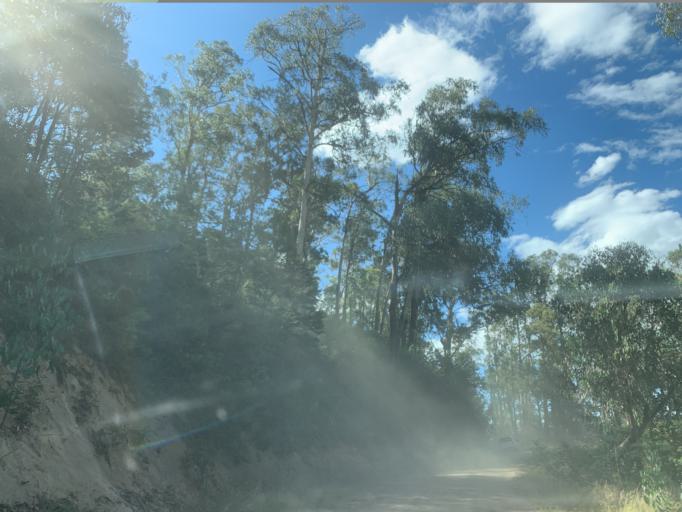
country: AU
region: Victoria
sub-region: Mansfield
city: Mansfield
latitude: -37.0930
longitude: 146.5185
